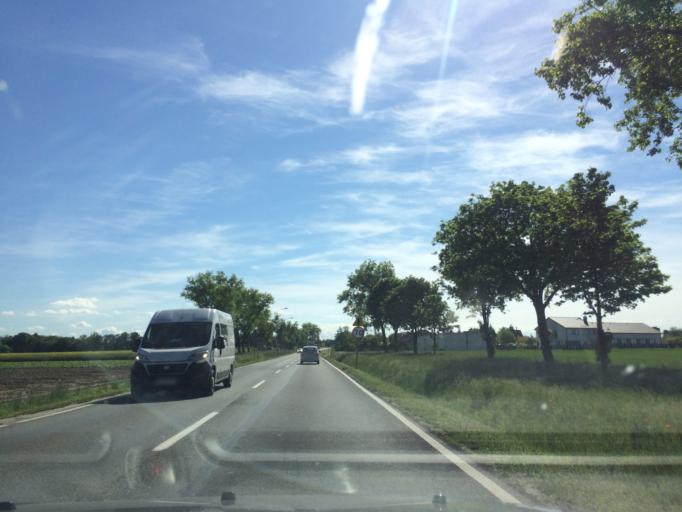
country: PL
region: Lower Silesian Voivodeship
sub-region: Powiat swidnicki
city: Swidnica
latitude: 50.8835
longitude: 16.5911
